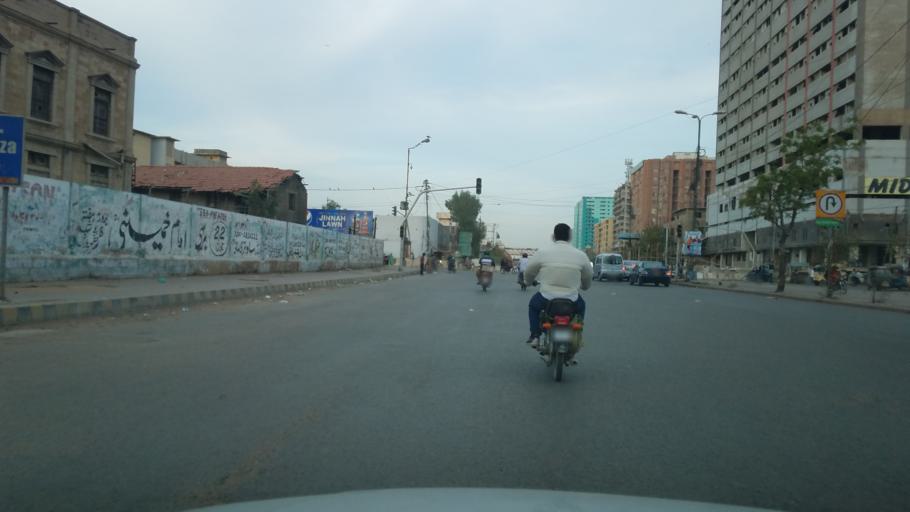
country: PK
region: Sindh
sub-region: Karachi District
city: Karachi
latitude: 24.8667
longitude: 67.0274
